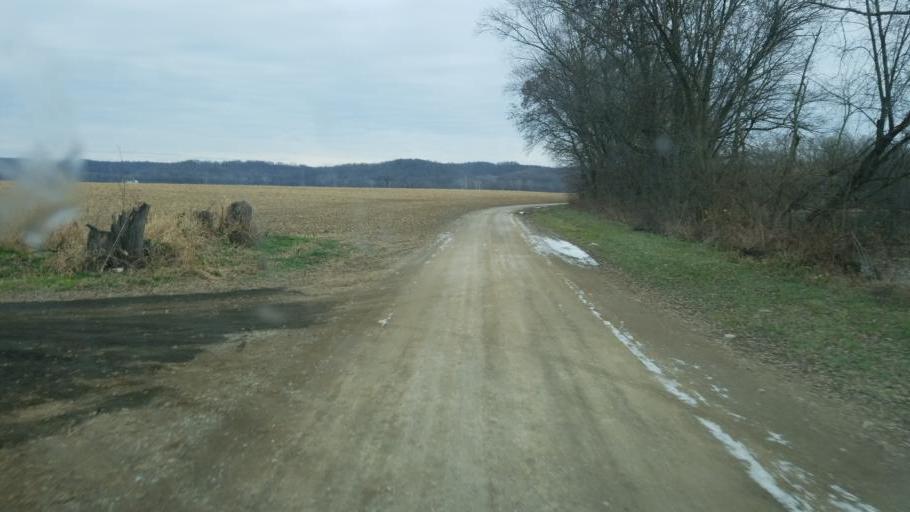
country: US
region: Ohio
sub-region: Muskingum County
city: Dresden
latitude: 40.1442
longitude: -81.9706
